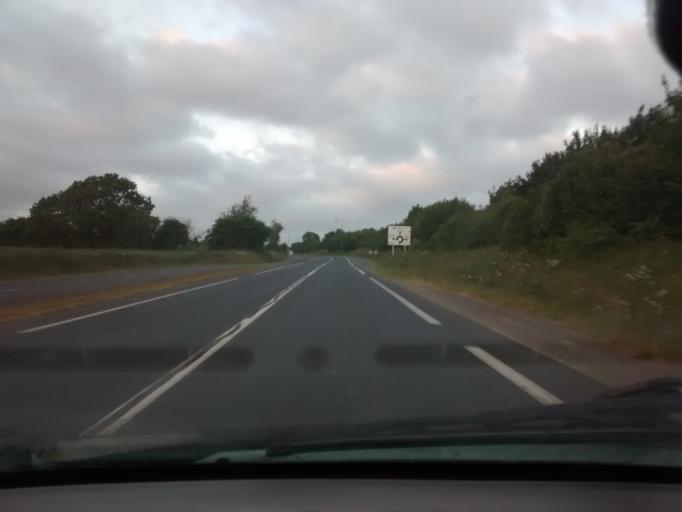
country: FR
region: Lower Normandy
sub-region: Departement de la Manche
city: Saint-Lo
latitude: 49.0990
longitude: -1.0976
